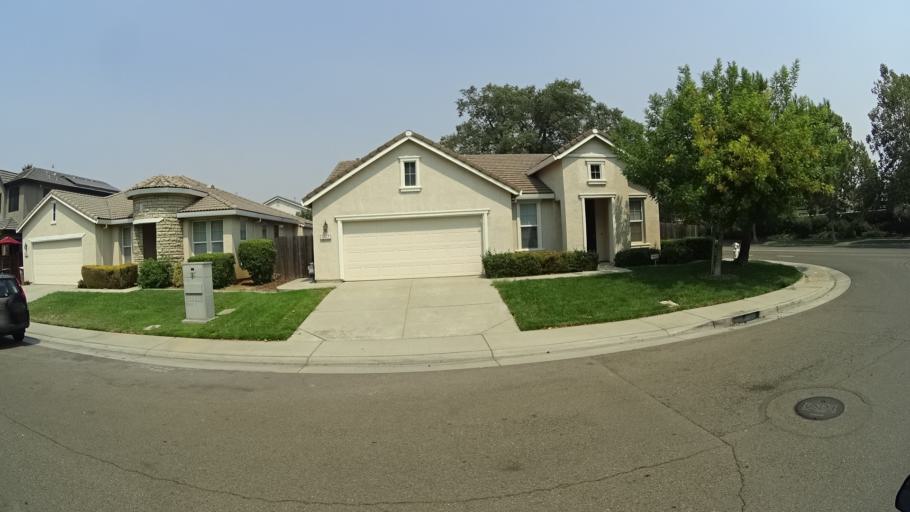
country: US
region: California
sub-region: Sacramento County
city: Laguna
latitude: 38.4028
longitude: -121.4410
